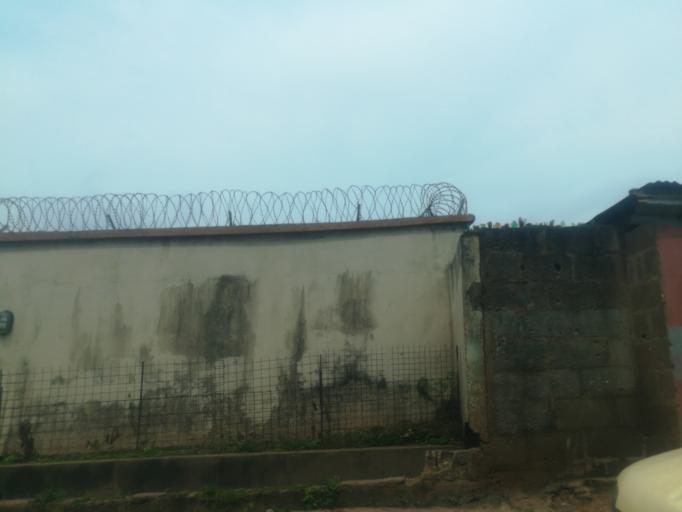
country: NG
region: Oyo
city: Ibadan
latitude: 7.4301
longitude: 3.9160
